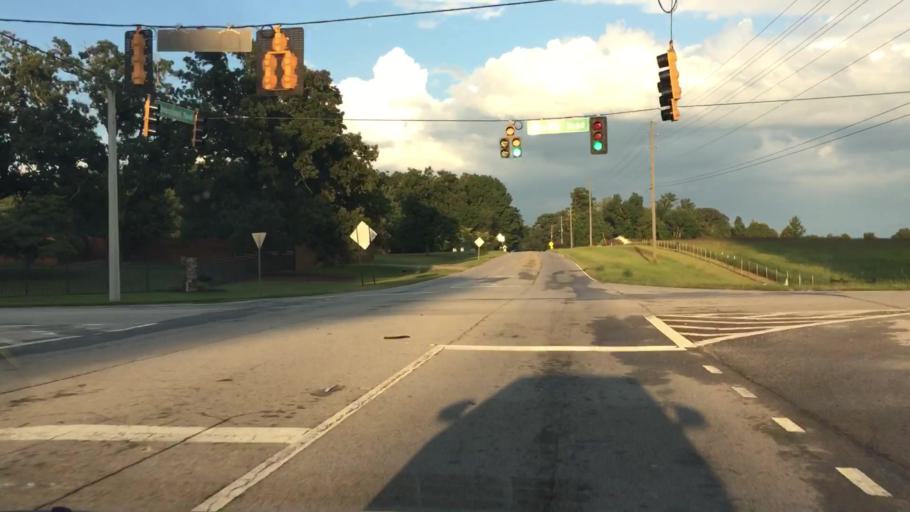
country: US
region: Georgia
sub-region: Henry County
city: McDonough
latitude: 33.4914
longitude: -84.1678
